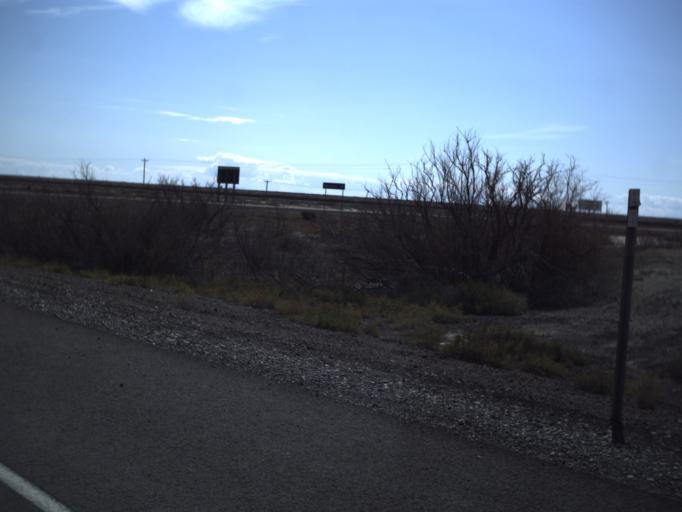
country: US
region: Utah
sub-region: Tooele County
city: Wendover
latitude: 40.7400
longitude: -113.9713
